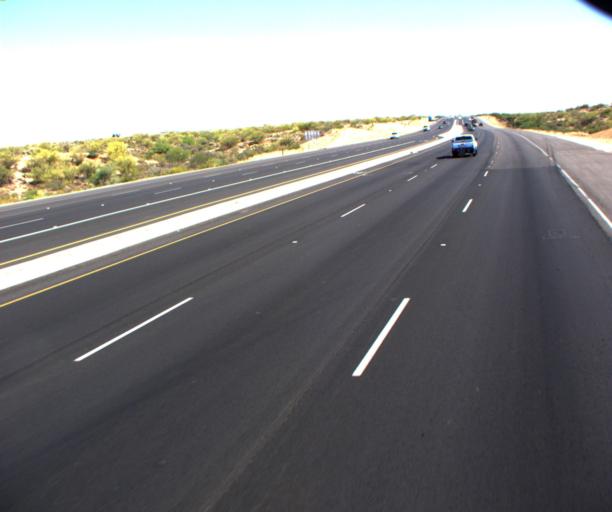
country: US
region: Arizona
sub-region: Pima County
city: Oro Valley
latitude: 32.4299
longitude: -110.9341
